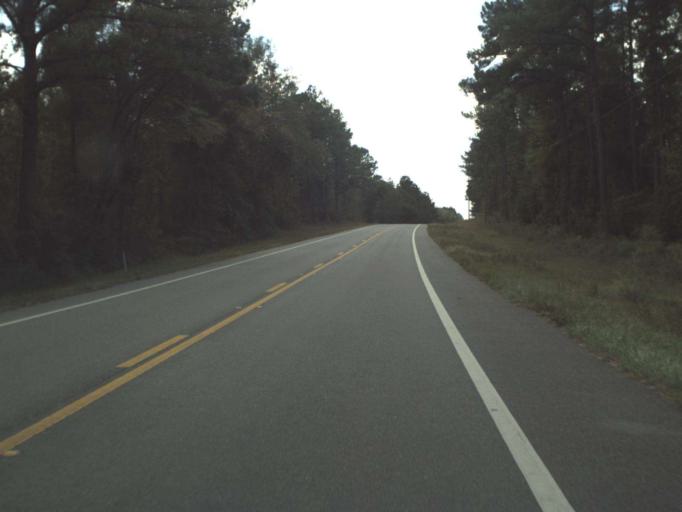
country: US
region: Florida
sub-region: Holmes County
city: Bonifay
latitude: 30.7106
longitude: -85.6184
